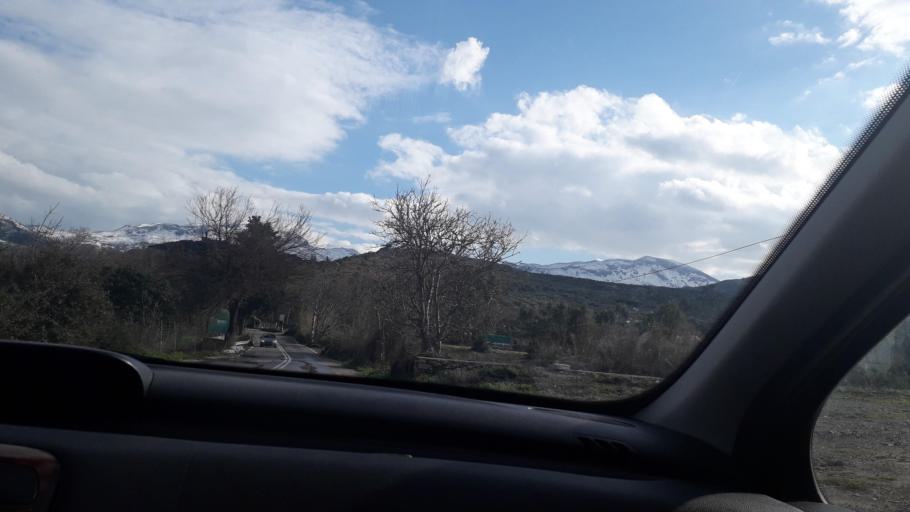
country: GR
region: Crete
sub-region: Nomos Rethymnis
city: Agia Foteini
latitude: 35.2906
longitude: 24.5606
